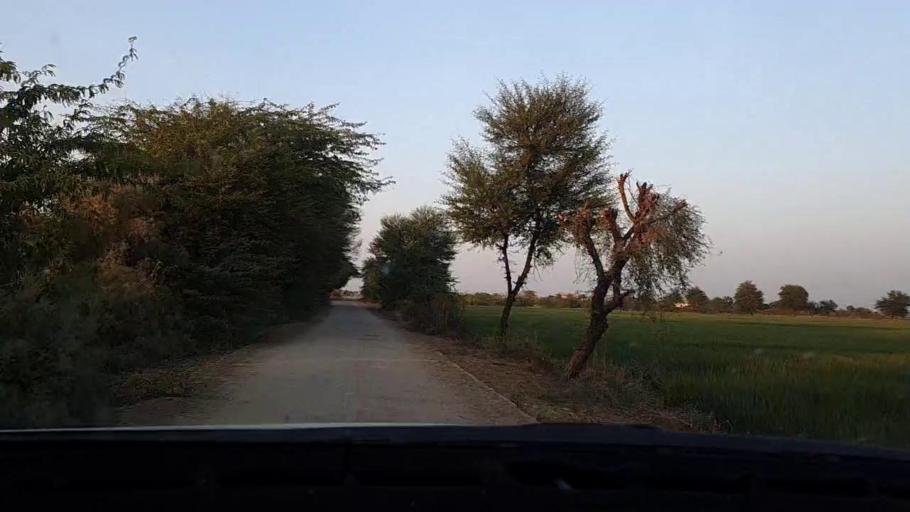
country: PK
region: Sindh
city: Tando Mittha Khan
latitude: 25.8490
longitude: 69.2304
